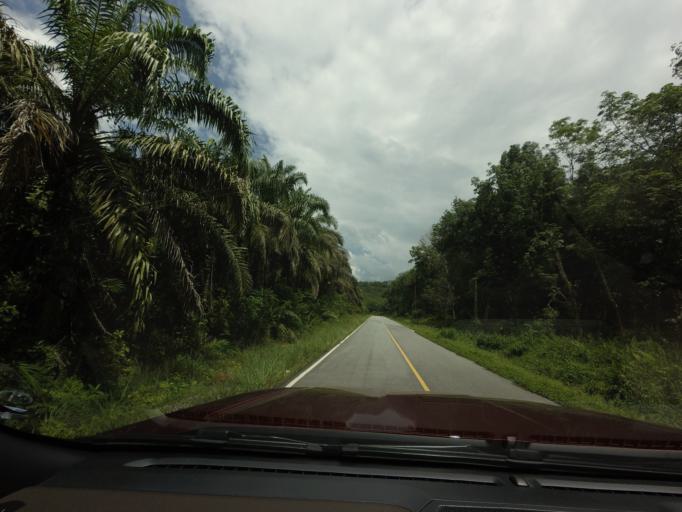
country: TH
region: Narathiwat
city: Chanae
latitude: 6.0528
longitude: 101.6877
